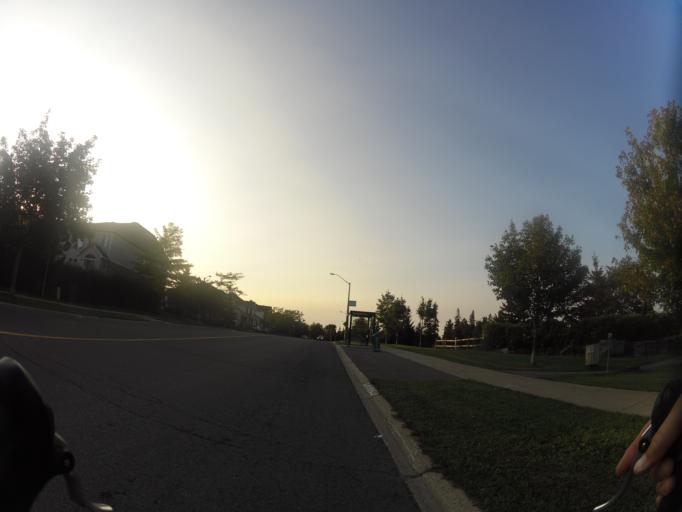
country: CA
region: Ontario
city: Bells Corners
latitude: 45.3501
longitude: -75.9408
